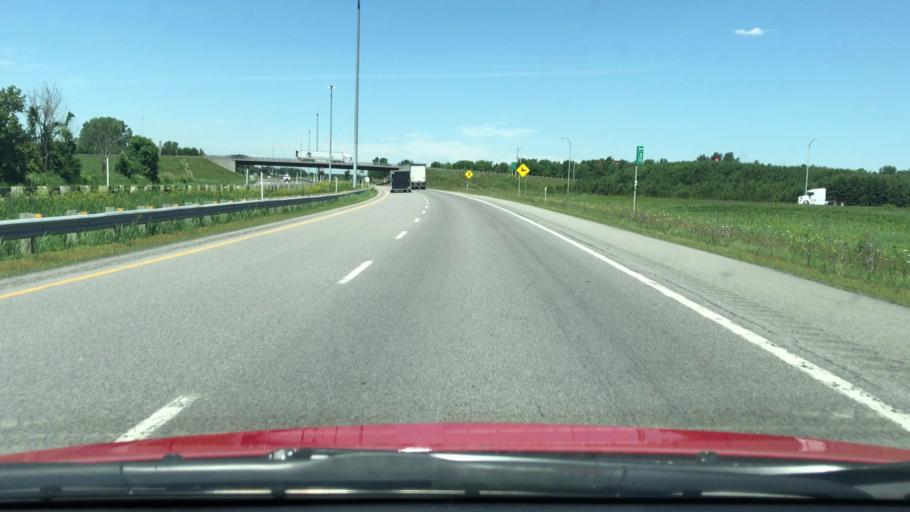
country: CA
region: Quebec
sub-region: Monteregie
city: Napierville
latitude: 45.1906
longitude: -73.4527
